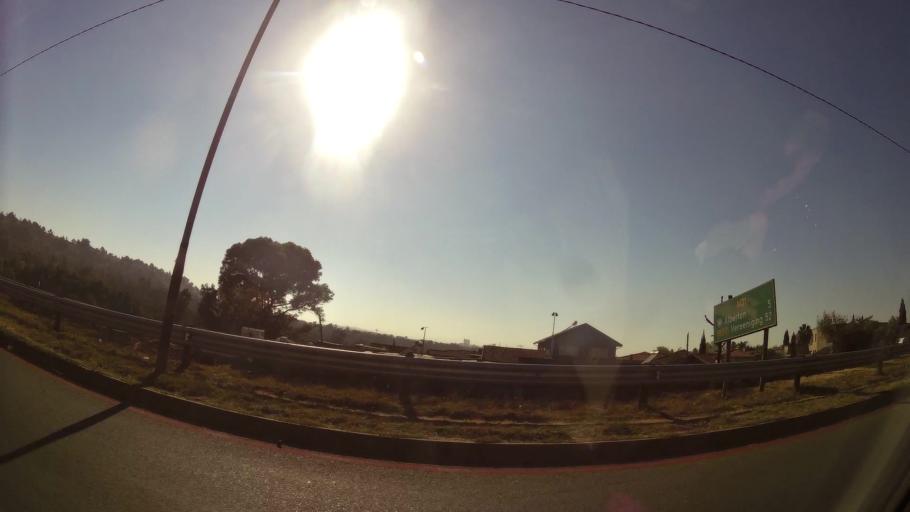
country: ZA
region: Gauteng
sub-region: City of Johannesburg Metropolitan Municipality
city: Johannesburg
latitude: -26.2382
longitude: 28.0987
